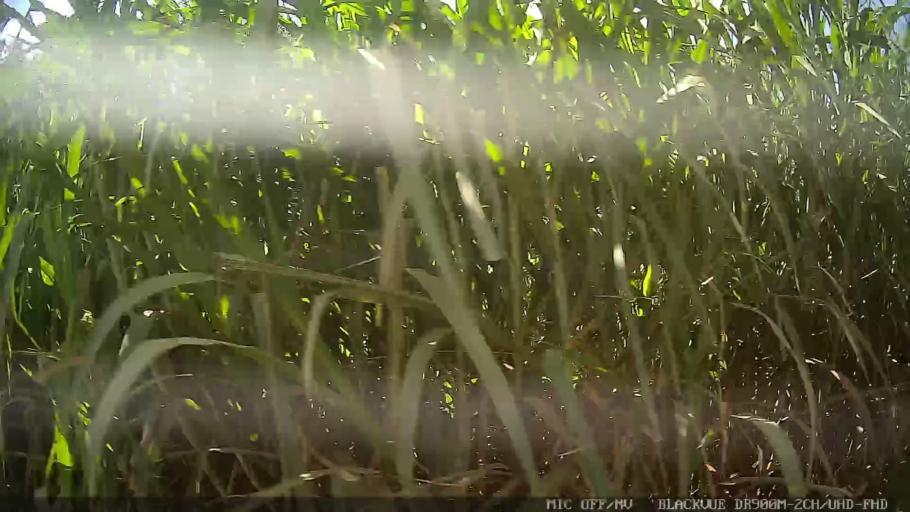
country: BR
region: Sao Paulo
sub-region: Braganca Paulista
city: Braganca Paulista
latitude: -22.9815
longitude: -46.6427
